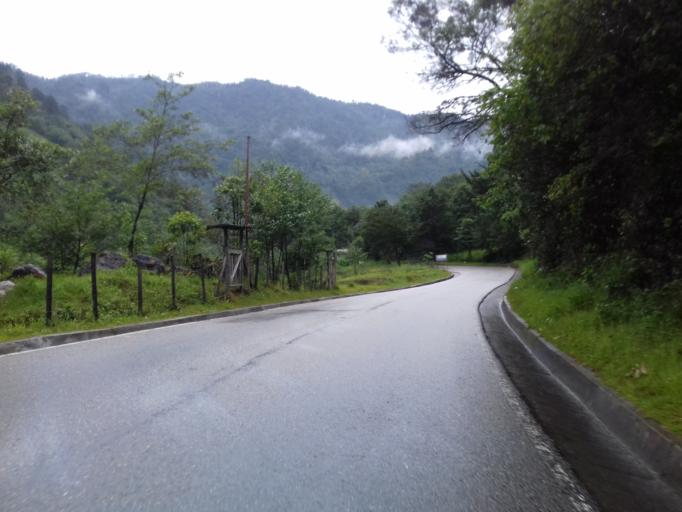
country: GT
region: Quiche
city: Nebaj
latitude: 15.3874
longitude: -91.1156
